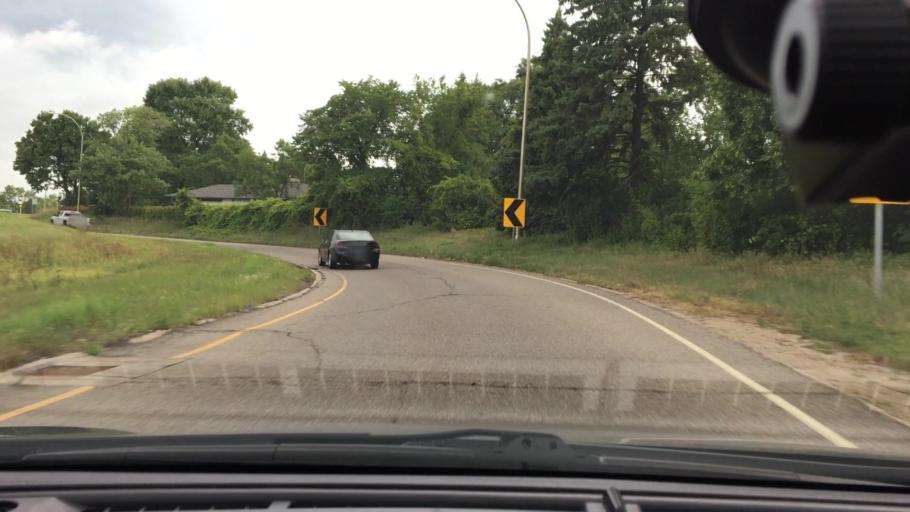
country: US
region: Minnesota
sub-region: Hennepin County
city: Edina
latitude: 44.8904
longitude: -93.3482
